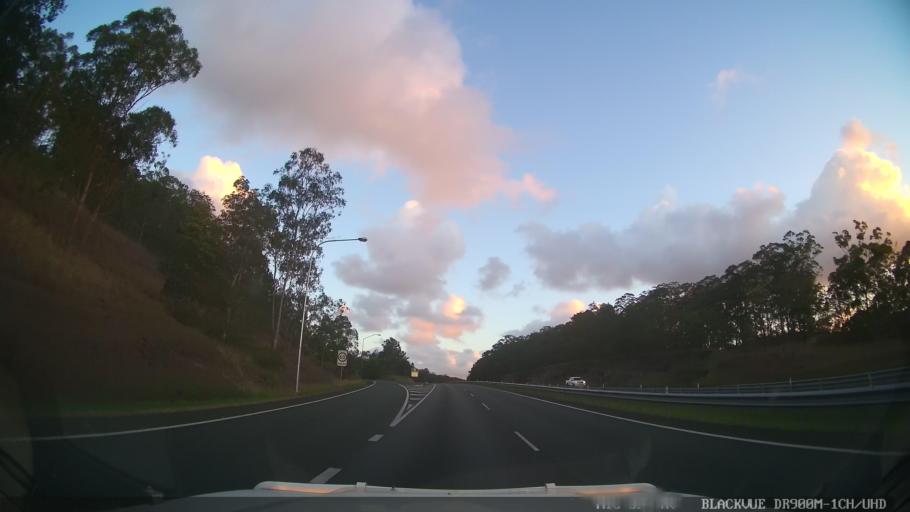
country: AU
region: Queensland
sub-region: Sunshine Coast
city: Yandina
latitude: -26.5906
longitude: 152.9695
